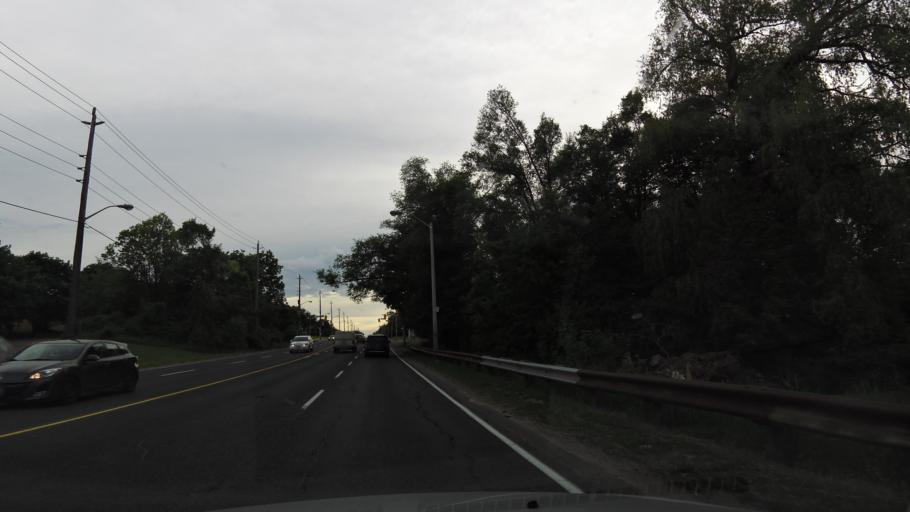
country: CA
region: Ontario
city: Etobicoke
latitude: 43.6815
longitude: -79.5313
